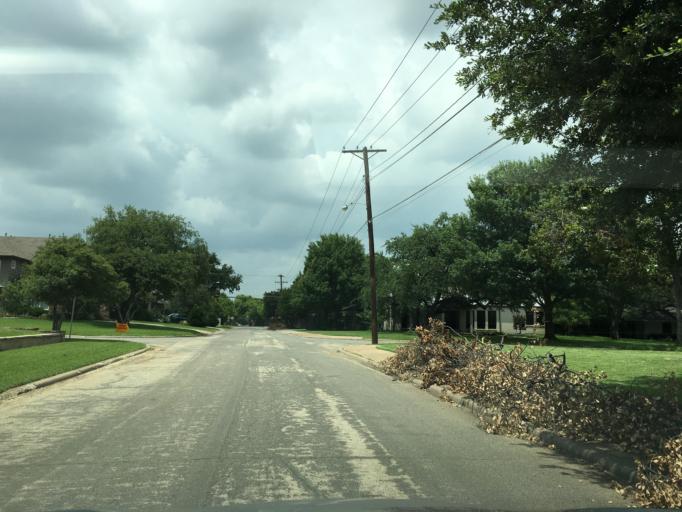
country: US
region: Texas
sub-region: Dallas County
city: University Park
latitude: 32.8984
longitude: -96.7838
